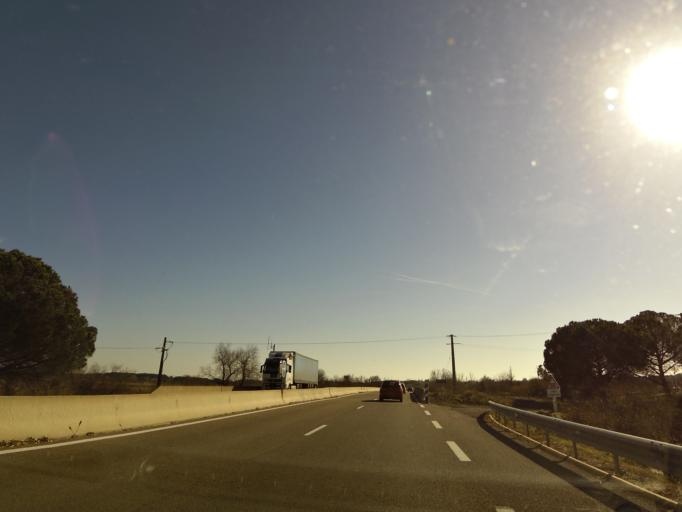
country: FR
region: Languedoc-Roussillon
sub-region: Departement du Gard
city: Aigues-Mortes
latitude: 43.5970
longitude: 4.1956
